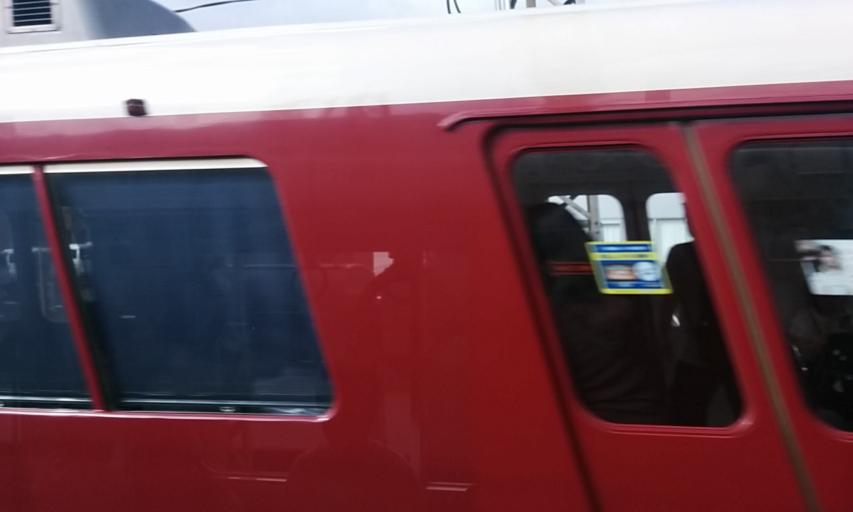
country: JP
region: Nara
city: Nara-shi
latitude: 34.6914
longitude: 135.7861
